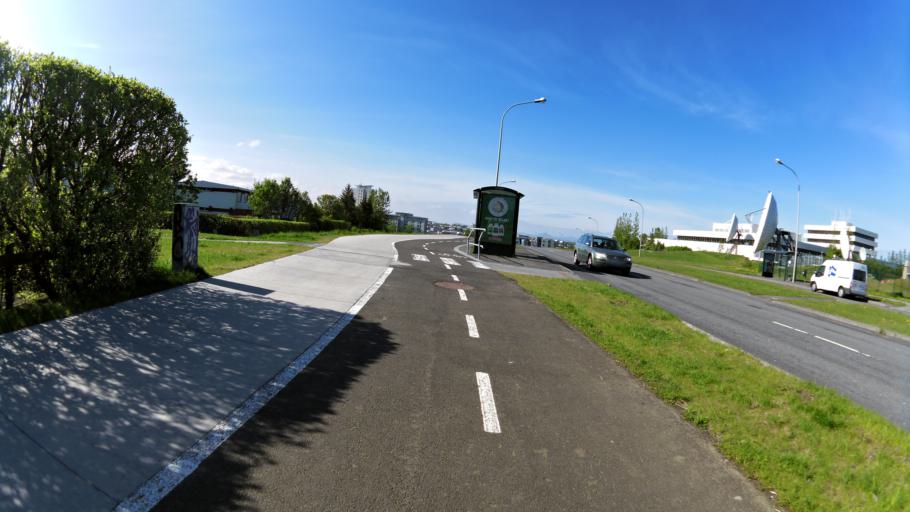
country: IS
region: Capital Region
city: Reykjavik
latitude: 64.1261
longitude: -21.8874
